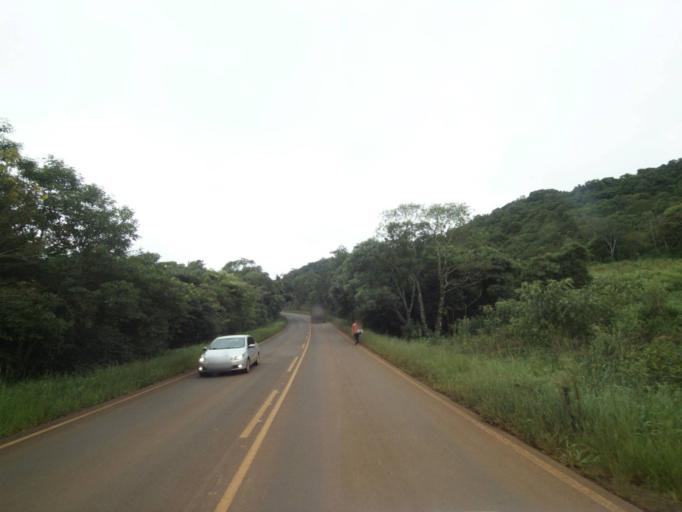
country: BR
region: Parana
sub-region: Pitanga
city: Pitanga
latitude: -24.9208
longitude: -51.8701
